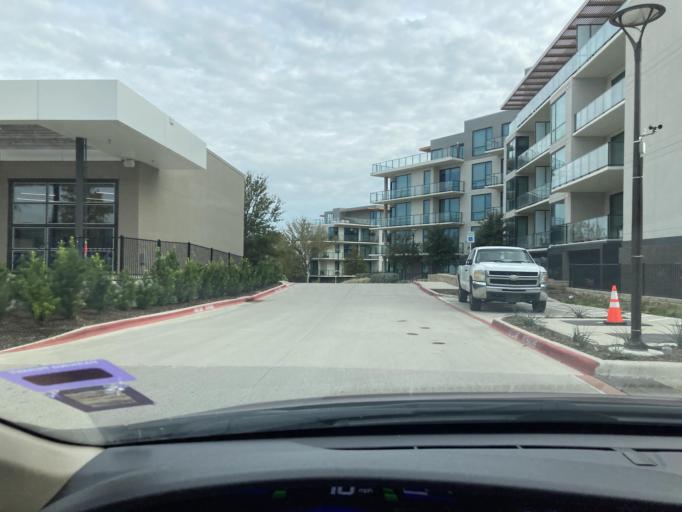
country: US
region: Texas
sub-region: Dallas County
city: University Park
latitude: 32.8594
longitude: -96.7642
